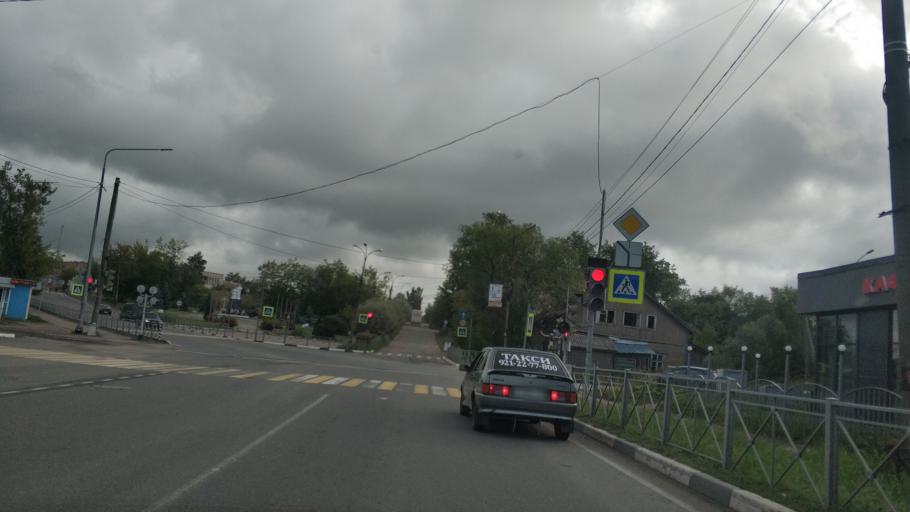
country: RU
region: Republic of Karelia
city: Sortavala
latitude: 61.7061
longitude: 30.6974
